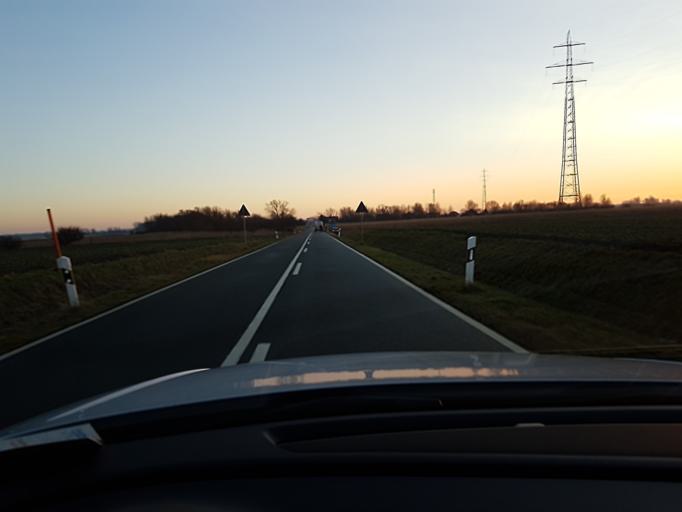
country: DE
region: Mecklenburg-Vorpommern
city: Wiek
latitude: 54.5629
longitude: 13.2476
